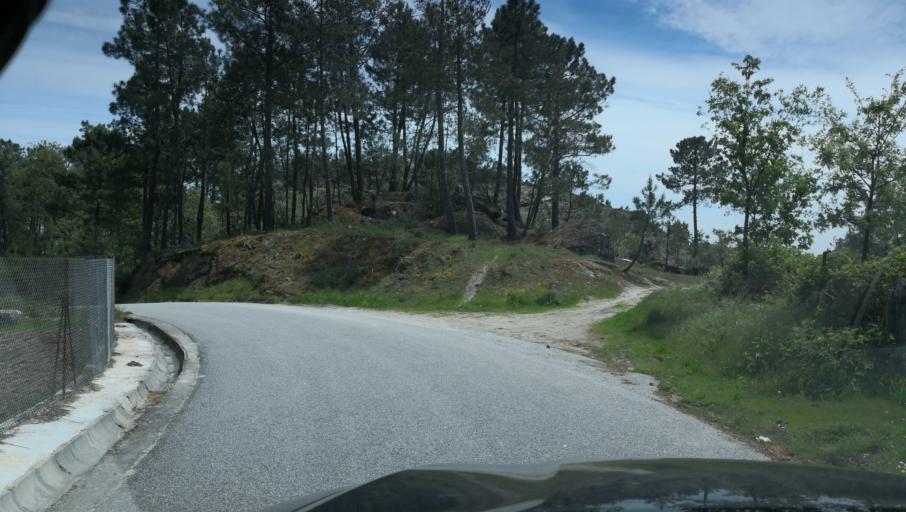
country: PT
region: Vila Real
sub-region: Vila Real
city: Vila Real
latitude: 41.3157
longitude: -7.7888
